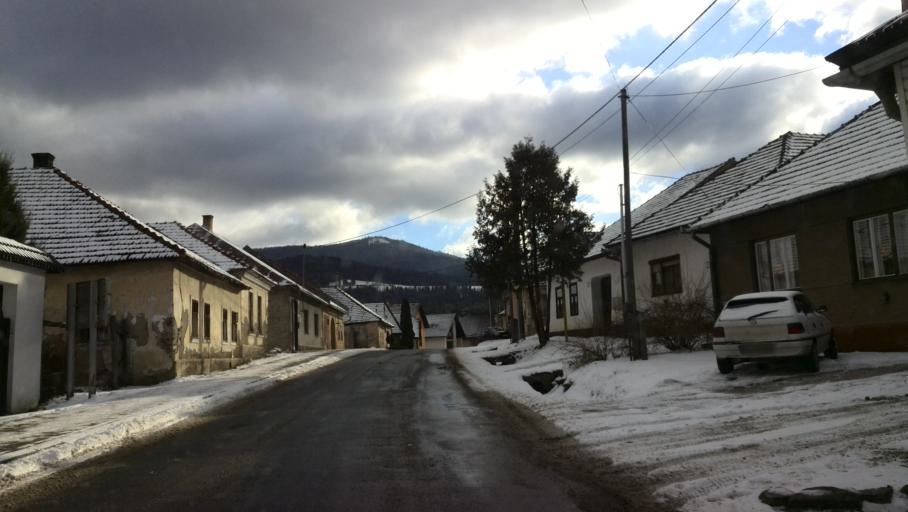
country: SK
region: Kosicky
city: Krompachy
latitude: 48.8038
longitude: 20.8054
